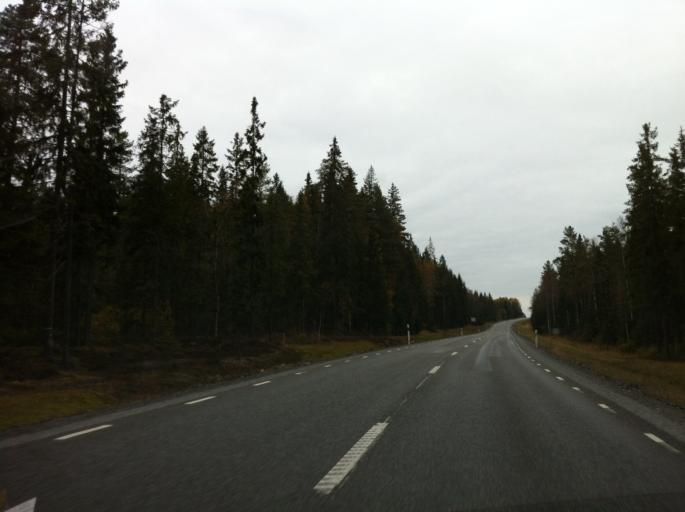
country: SE
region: OErebro
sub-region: Ljusnarsbergs Kommun
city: Kopparberg
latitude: 59.9175
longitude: 15.0221
